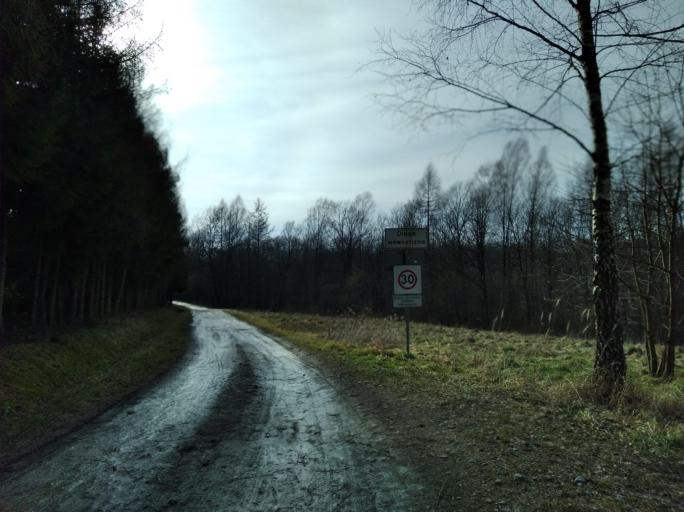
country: PL
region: Subcarpathian Voivodeship
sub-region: Powiat brzozowski
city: Grabownica Starzenska
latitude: 49.6449
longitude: 22.0657
